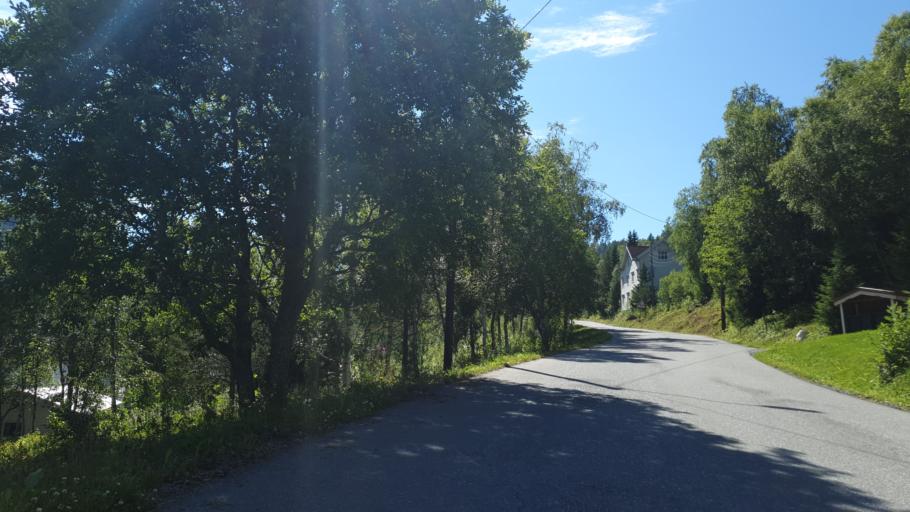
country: NO
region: Sor-Trondelag
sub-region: Meldal
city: Meldal
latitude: 63.1249
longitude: 9.7035
